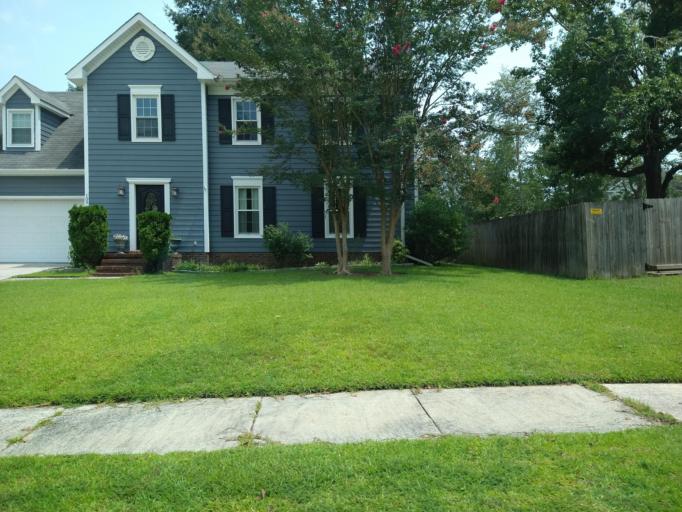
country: US
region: North Carolina
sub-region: Onslow County
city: Pumpkin Center
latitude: 34.7635
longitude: -77.3718
